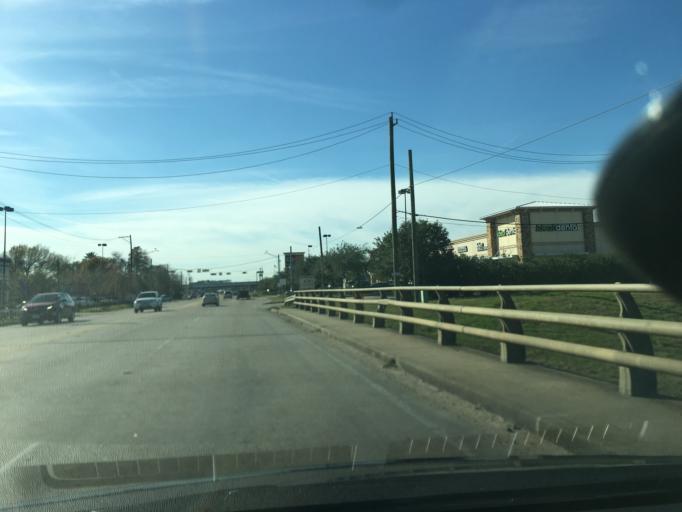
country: US
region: Texas
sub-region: Harris County
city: Cloverleaf
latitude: 29.8100
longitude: -95.1586
